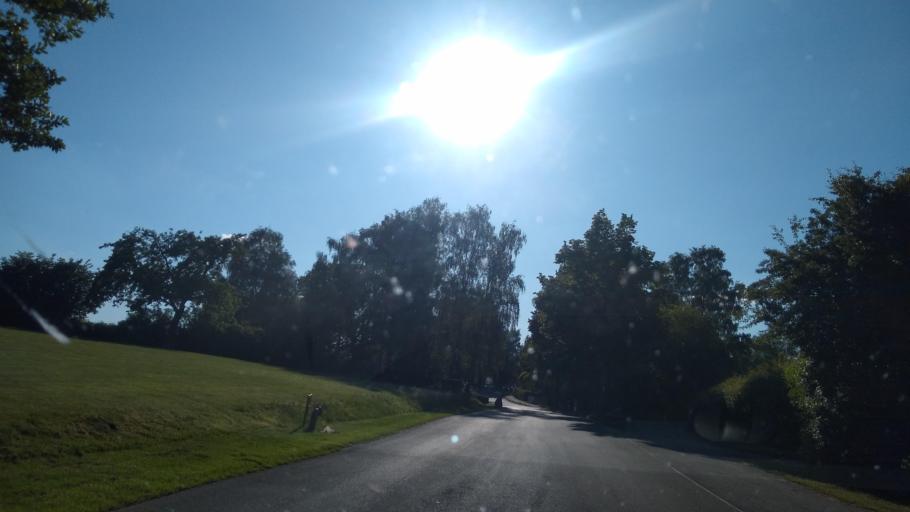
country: DE
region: Schleswig-Holstein
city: Neudorf-Bornstein
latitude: 54.4165
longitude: 9.9321
